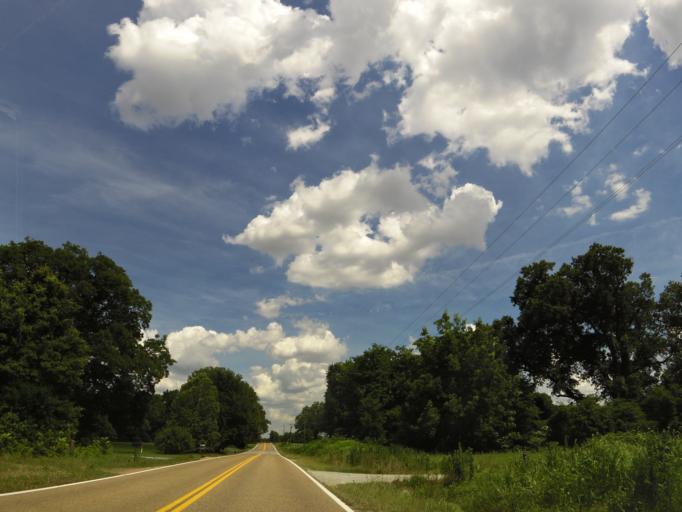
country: US
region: Tennessee
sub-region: Gibson County
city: Dyer
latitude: 35.9995
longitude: -89.1301
